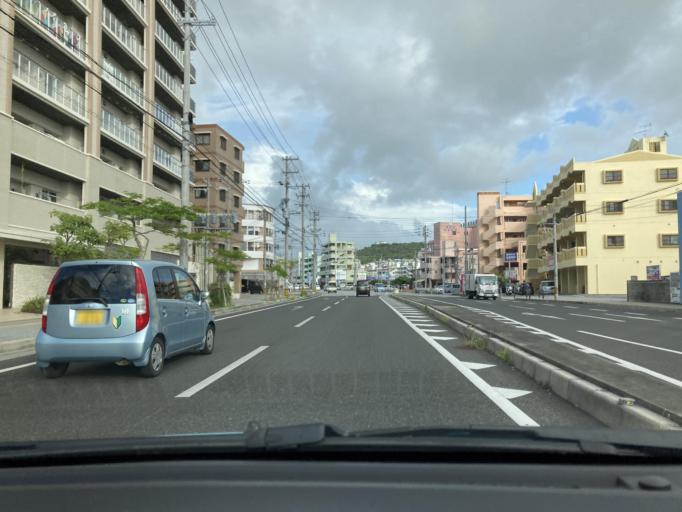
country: JP
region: Okinawa
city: Tomigusuku
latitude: 26.1771
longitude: 127.6739
